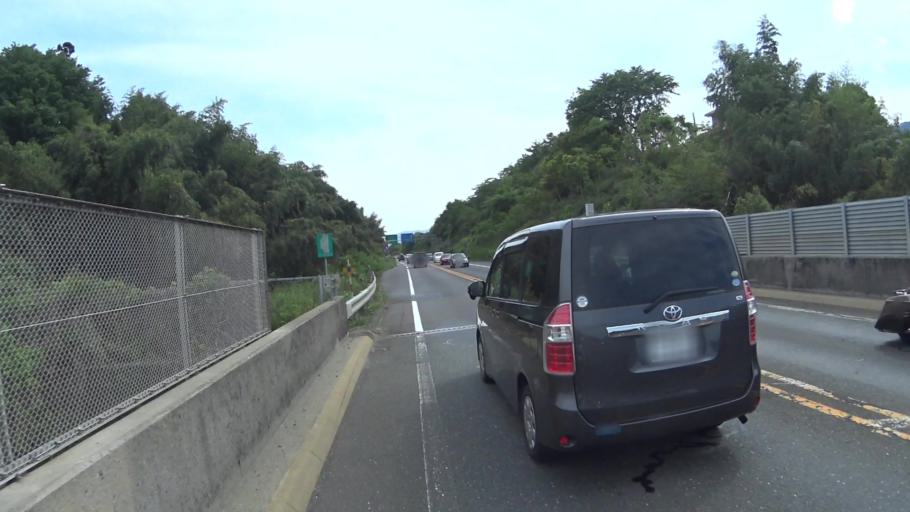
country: JP
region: Shiga Prefecture
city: Otsu-shi
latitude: 35.0851
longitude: 135.8846
